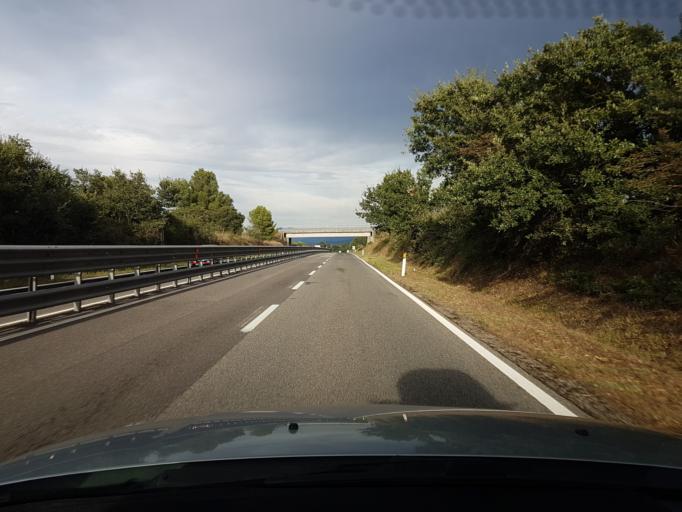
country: IT
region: Sardinia
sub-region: Provincia di Oristano
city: Ghilarza
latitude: 40.1155
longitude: 8.8293
